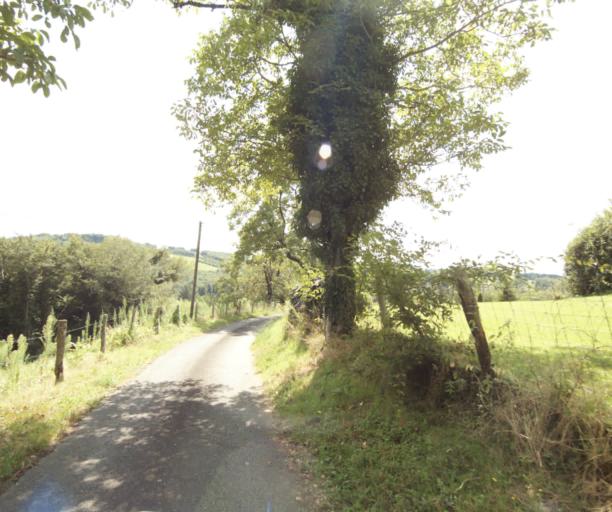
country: FR
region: Limousin
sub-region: Departement de la Correze
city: Sainte-Fortunade
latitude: 45.1719
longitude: 1.8277
